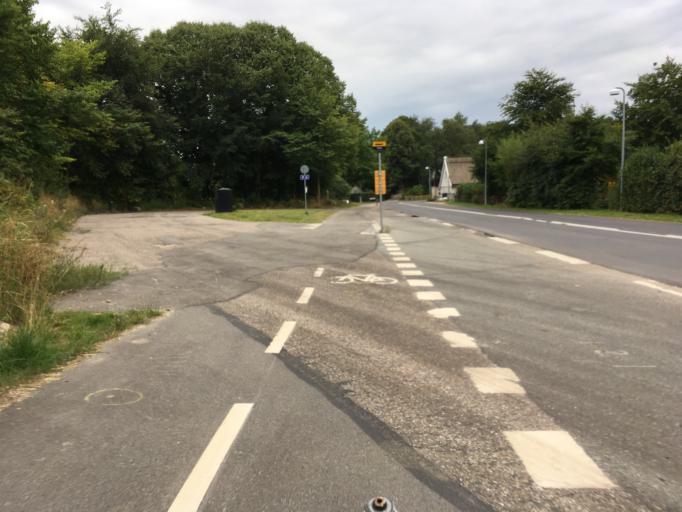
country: DK
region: Capital Region
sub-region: Hillerod Kommune
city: Skaevinge
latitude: 55.9197
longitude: 12.2033
